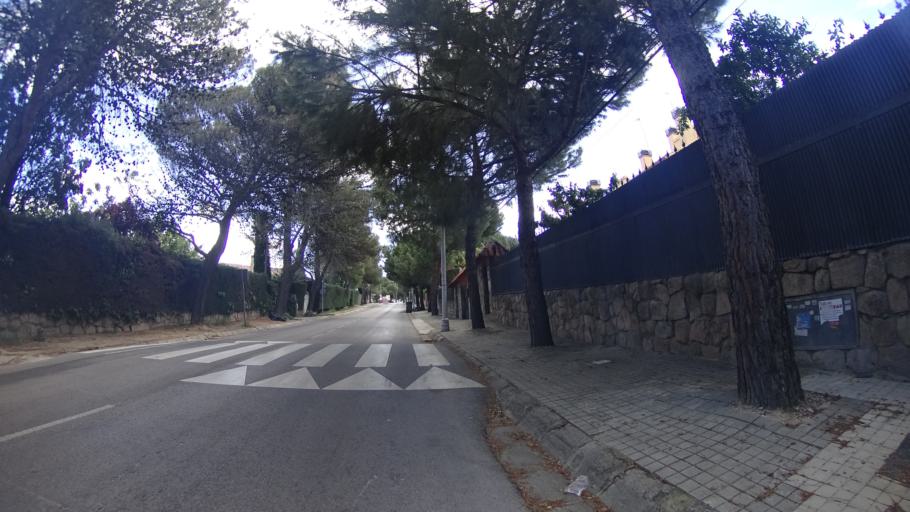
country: ES
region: Madrid
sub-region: Provincia de Madrid
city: Villaviciosa de Odon
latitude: 40.3721
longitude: -3.9262
